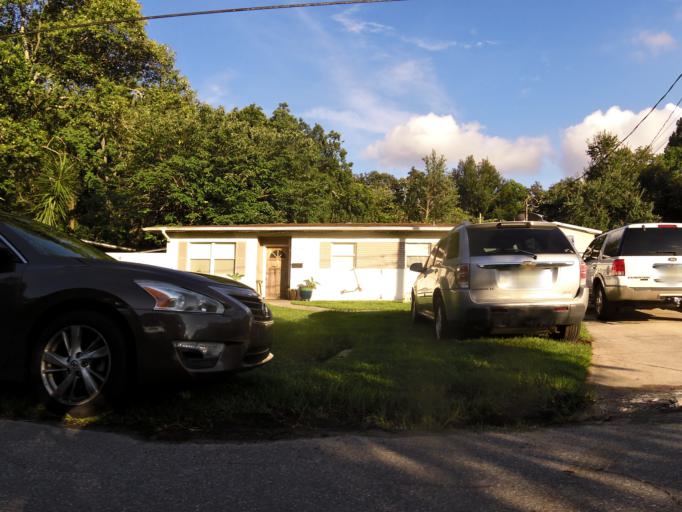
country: US
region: Florida
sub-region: Duval County
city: Jacksonville
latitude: 30.2966
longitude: -81.6255
